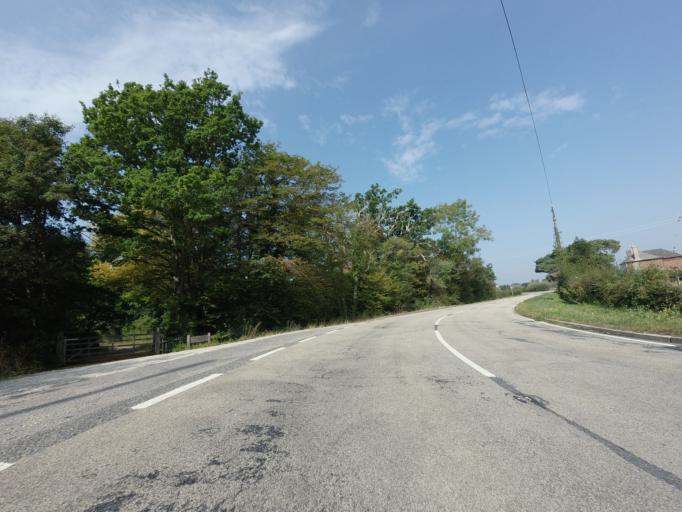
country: GB
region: England
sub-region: Kent
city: Headcorn
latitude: 51.1173
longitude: 0.6107
